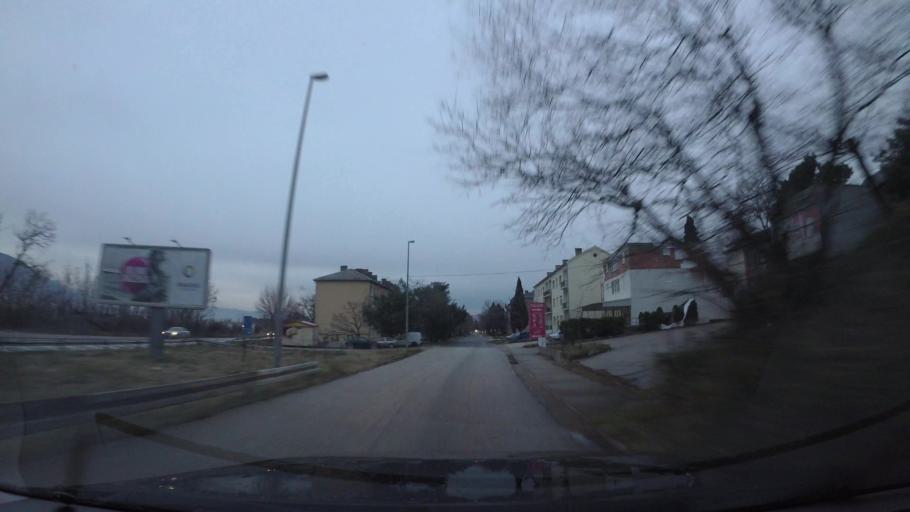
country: BA
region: Federation of Bosnia and Herzegovina
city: Rodoc
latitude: 43.3235
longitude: 17.8200
